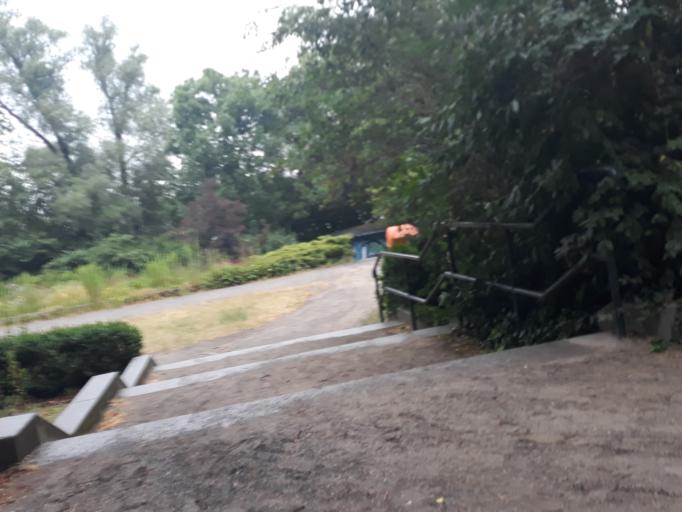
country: DE
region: Berlin
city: Weissensee
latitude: 52.5522
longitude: 13.4631
